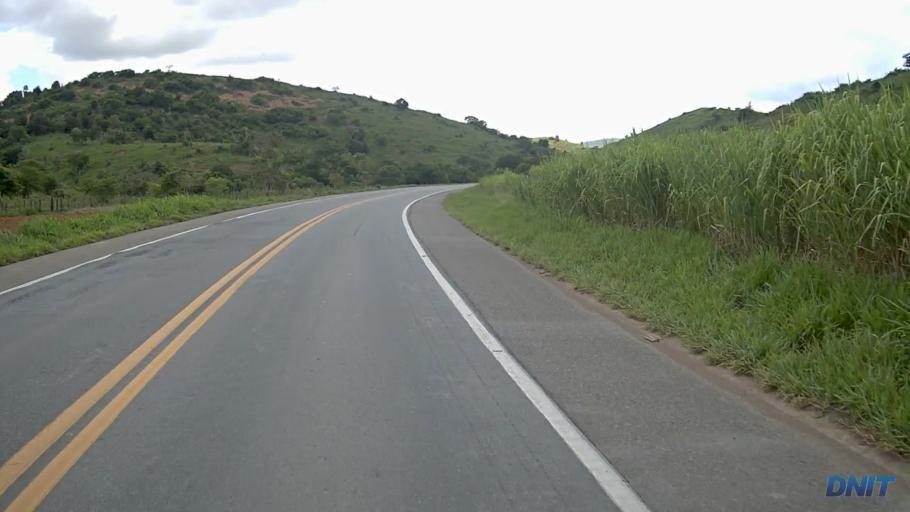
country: BR
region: Minas Gerais
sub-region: Governador Valadares
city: Governador Valadares
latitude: -18.9666
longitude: -42.0899
